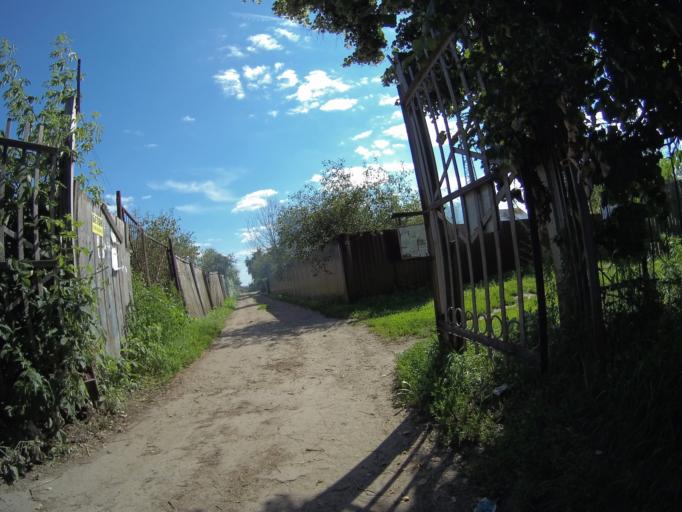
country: RU
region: Vladimir
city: Vorsha
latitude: 56.0990
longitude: 40.2164
